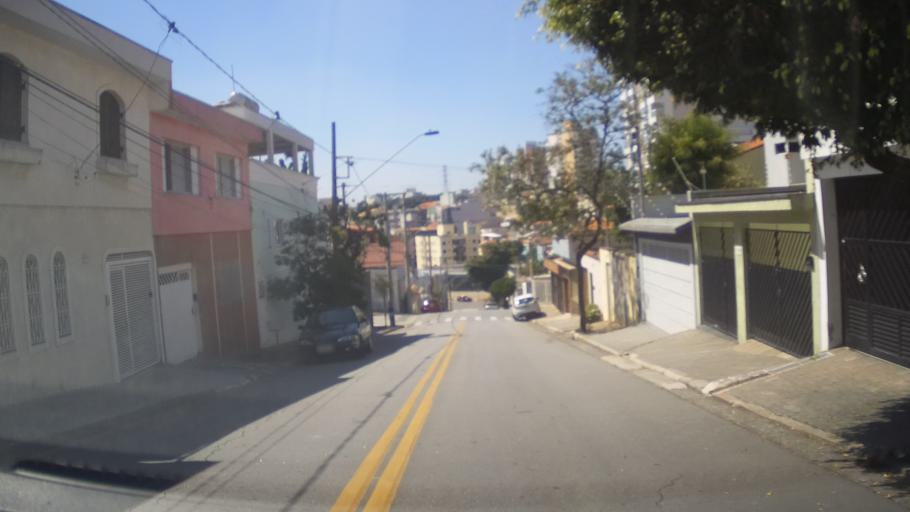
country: BR
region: Sao Paulo
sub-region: Sao Caetano Do Sul
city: Sao Caetano do Sul
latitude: -23.6231
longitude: -46.5593
